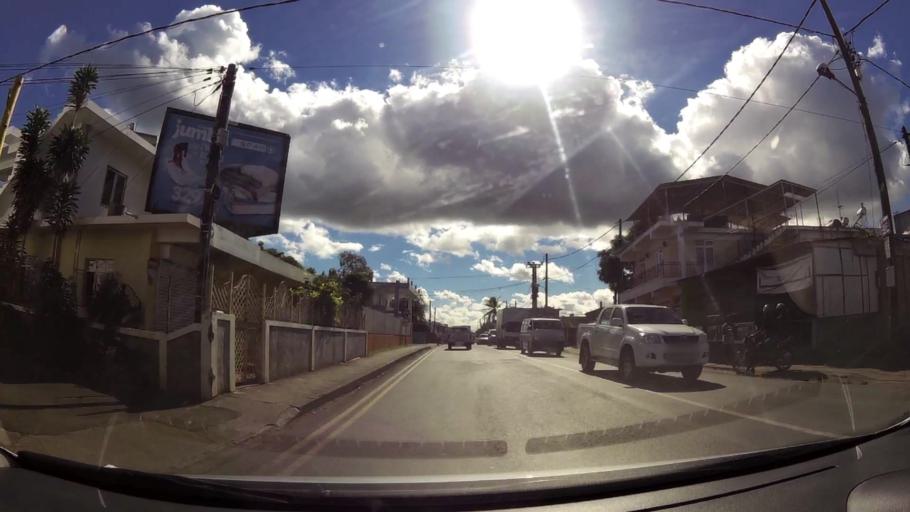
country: MU
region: Pamplemousses
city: Terre Rouge
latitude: -20.1326
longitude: 57.5287
